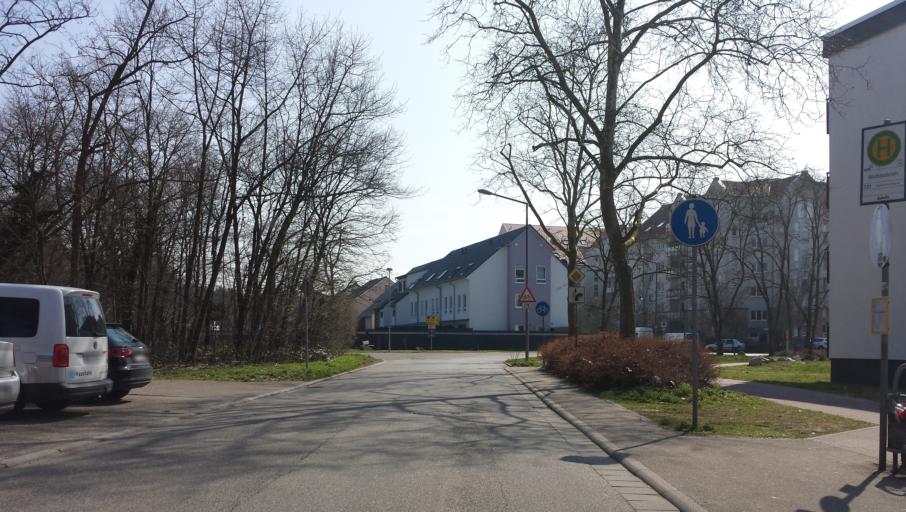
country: DE
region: Baden-Wuerttemberg
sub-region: Karlsruhe Region
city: Hockenheim
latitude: 49.3192
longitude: 8.5636
